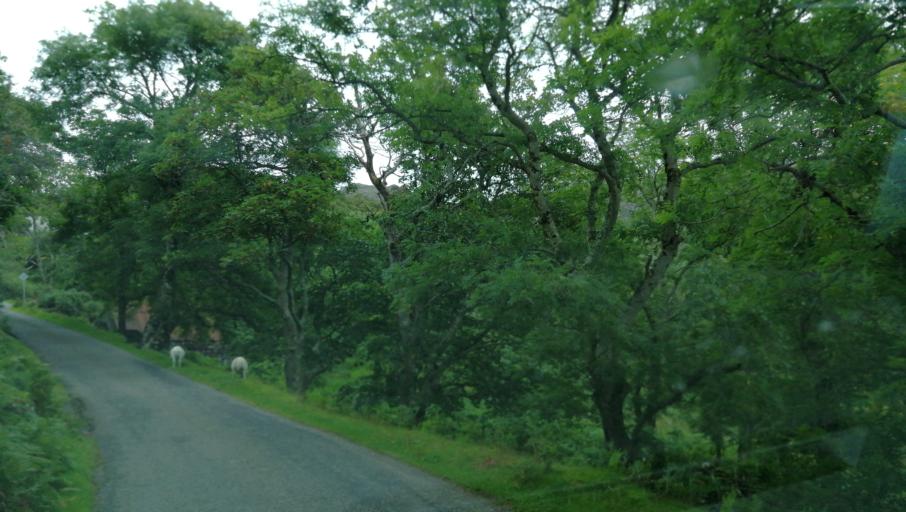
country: GB
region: Scotland
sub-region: Highland
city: Ullapool
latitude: 58.1362
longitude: -5.2494
